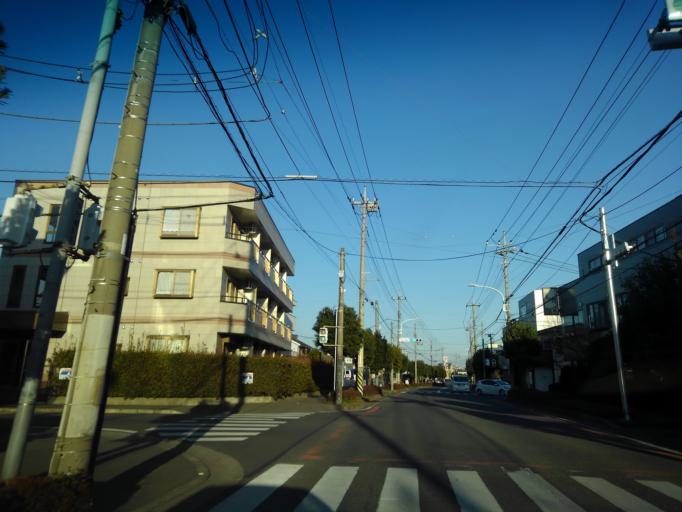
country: JP
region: Saitama
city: Tokorozawa
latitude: 35.7986
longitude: 139.5155
